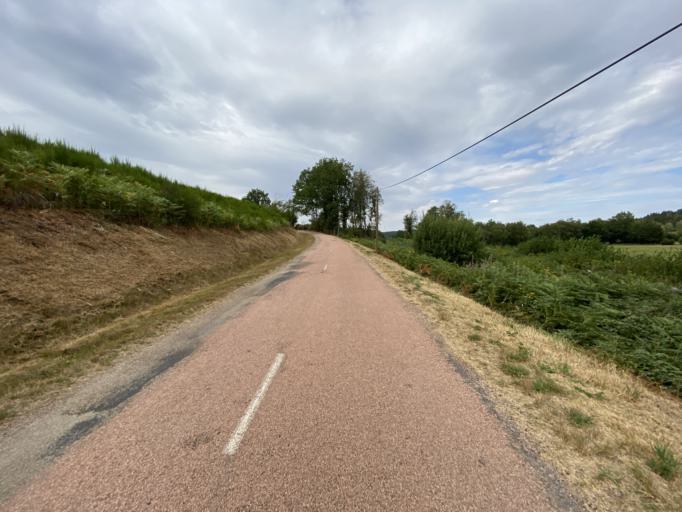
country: FR
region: Bourgogne
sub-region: Departement de la Cote-d'Or
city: Saulieu
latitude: 47.2754
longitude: 4.1386
